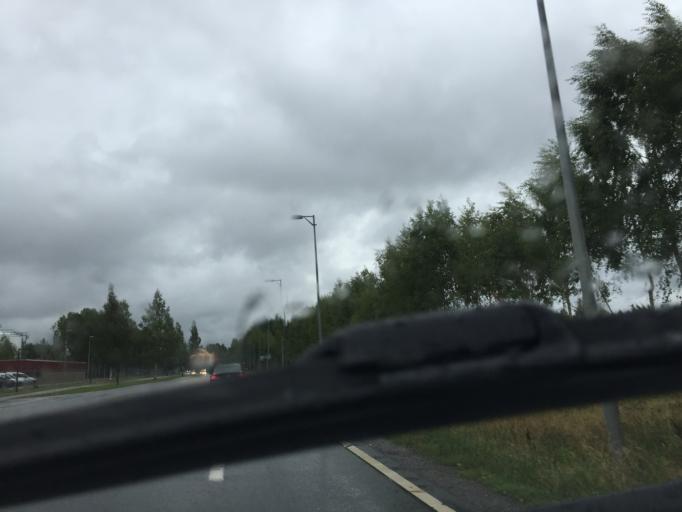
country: NO
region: Akershus
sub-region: Nannestad
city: Teigebyen
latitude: 60.1812
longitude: 11.0850
